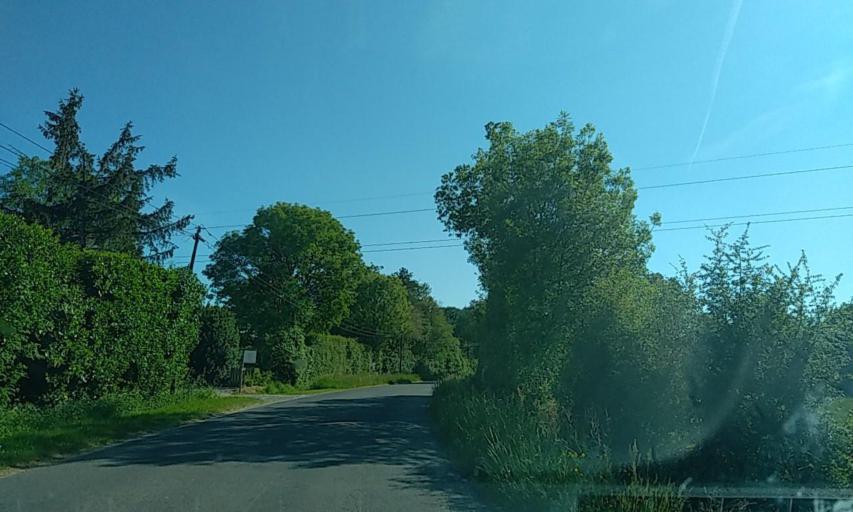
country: FR
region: Poitou-Charentes
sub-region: Departement des Deux-Sevres
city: Boisme
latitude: 46.7972
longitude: -0.4230
